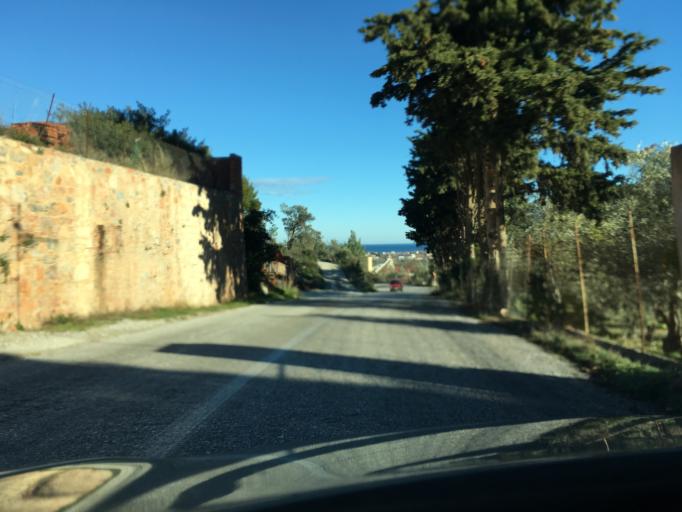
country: GR
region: Thessaly
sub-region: Nomos Magnisias
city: Skopelos
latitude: 39.1031
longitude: 23.7217
